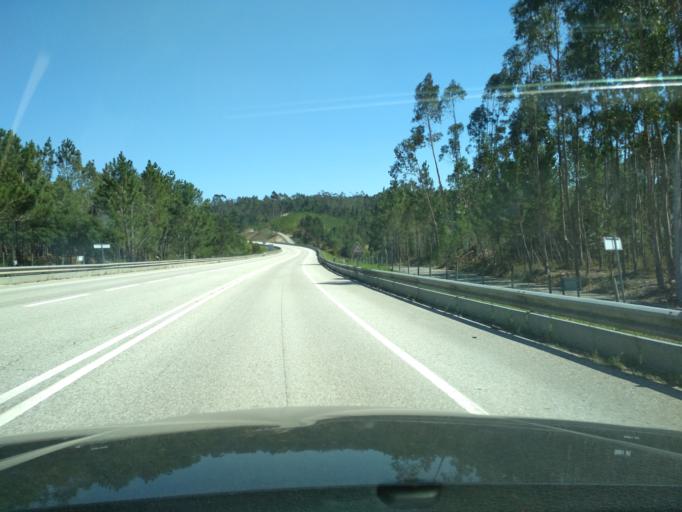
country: PT
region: Leiria
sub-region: Pombal
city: Lourical
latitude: 39.9871
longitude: -8.7680
